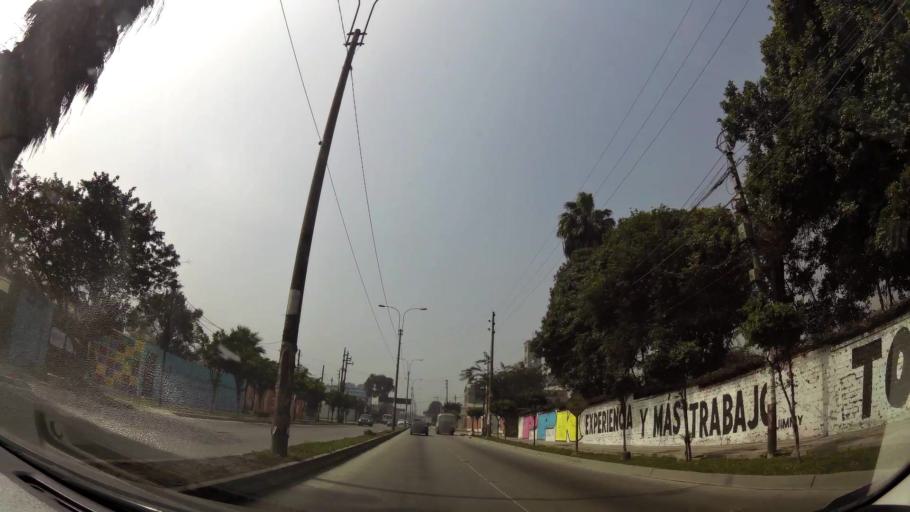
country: PE
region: Lima
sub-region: Lima
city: Chosica
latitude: -11.9482
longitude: -76.7185
